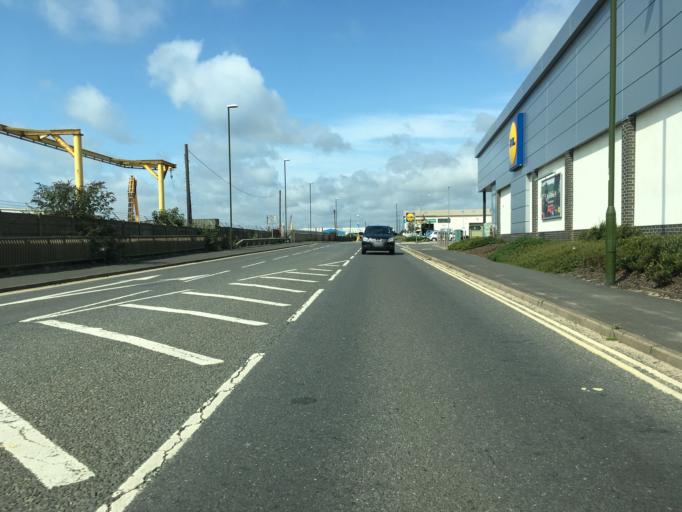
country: GB
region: England
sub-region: West Sussex
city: Shoreham-by-Sea
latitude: 50.8324
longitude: -0.2564
